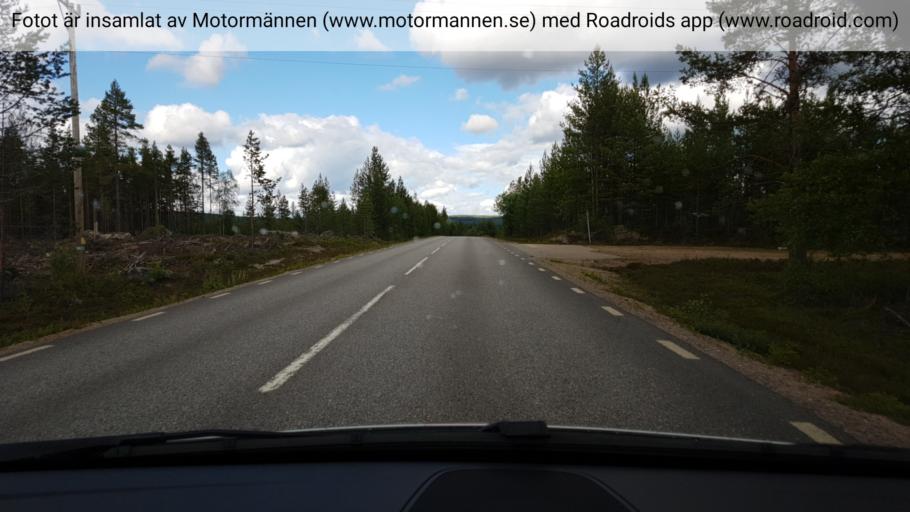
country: SE
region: Jaemtland
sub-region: Harjedalens Kommun
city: Sveg
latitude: 62.0351
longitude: 14.7334
